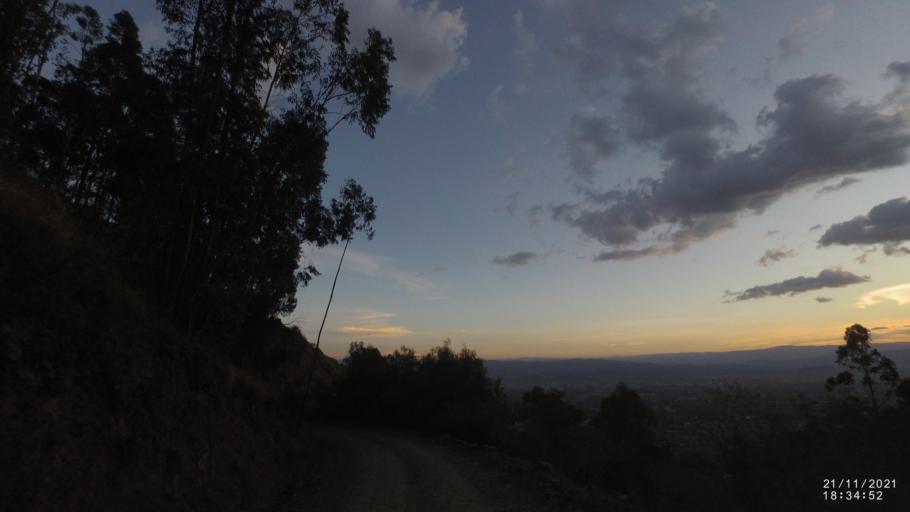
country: BO
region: Cochabamba
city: Cochabamba
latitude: -17.3107
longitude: -66.2199
